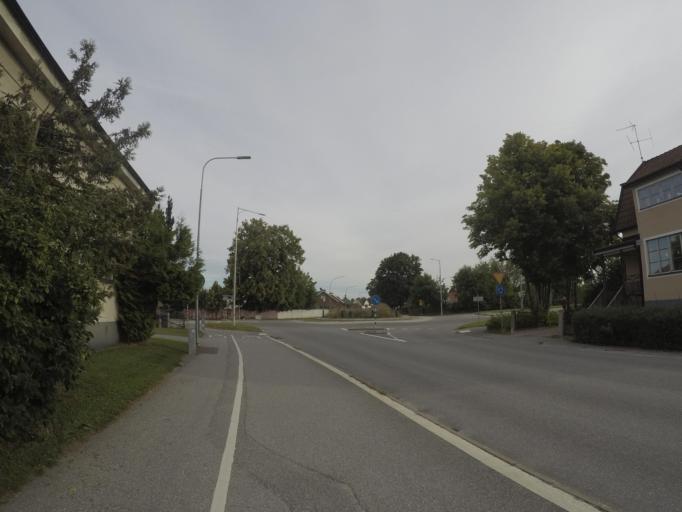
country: SE
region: OErebro
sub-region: Orebro Kommun
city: Orebro
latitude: 59.2614
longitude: 15.2484
